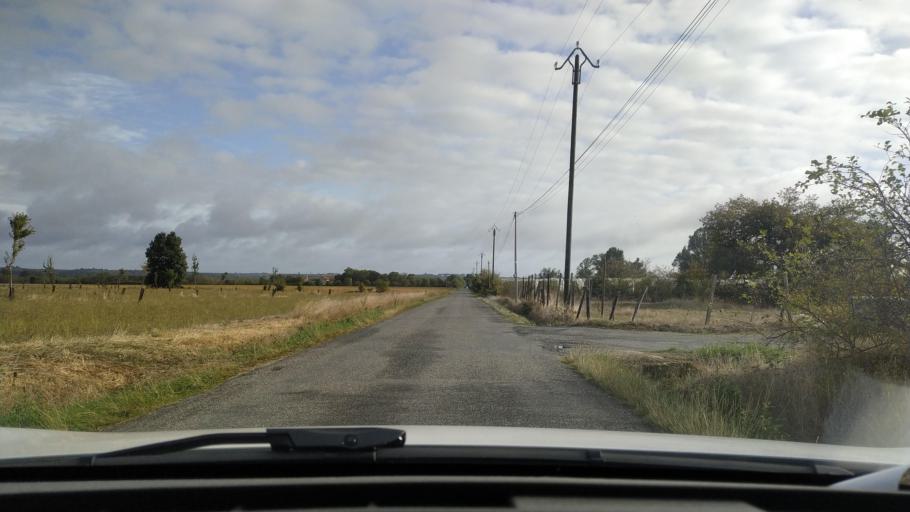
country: FR
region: Midi-Pyrenees
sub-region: Departement de la Haute-Garonne
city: Cintegabelle
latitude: 43.2849
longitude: 1.5116
